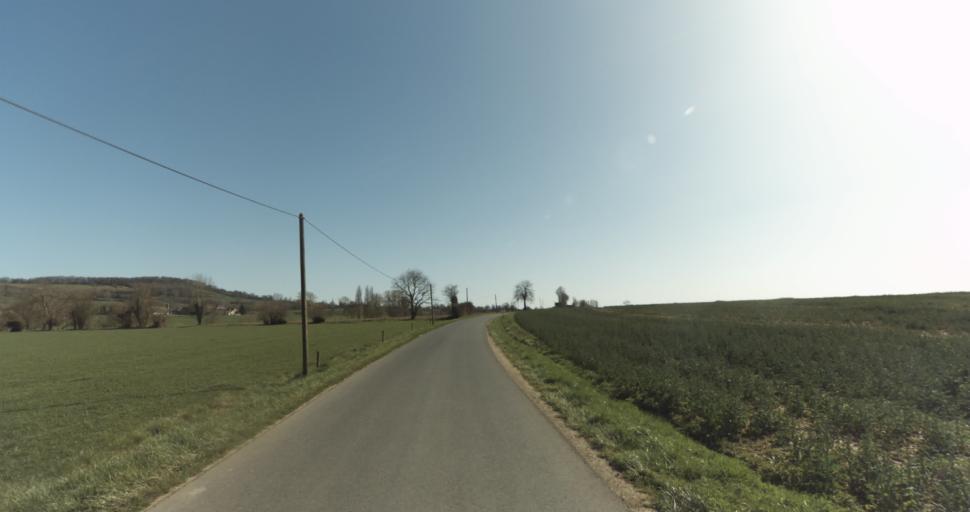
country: FR
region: Lower Normandy
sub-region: Departement de l'Orne
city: Trun
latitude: 48.9081
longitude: 0.0344
